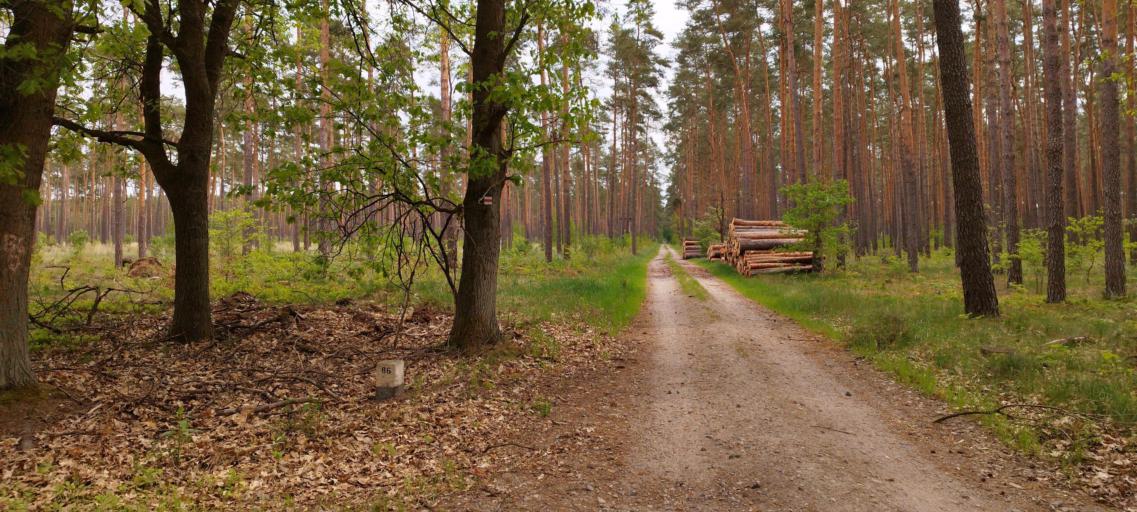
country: DE
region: Brandenburg
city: Spreenhagen
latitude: 52.3857
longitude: 13.9029
